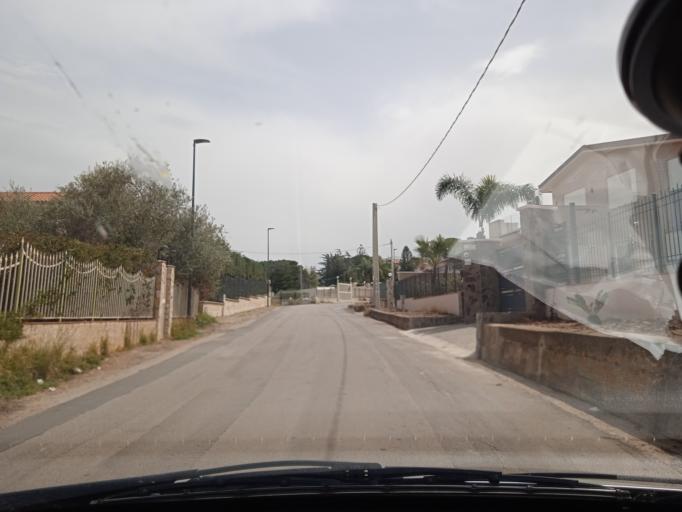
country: IT
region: Sicily
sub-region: Palermo
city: Torre Colonna-Sperone
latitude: 38.0262
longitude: 13.5756
